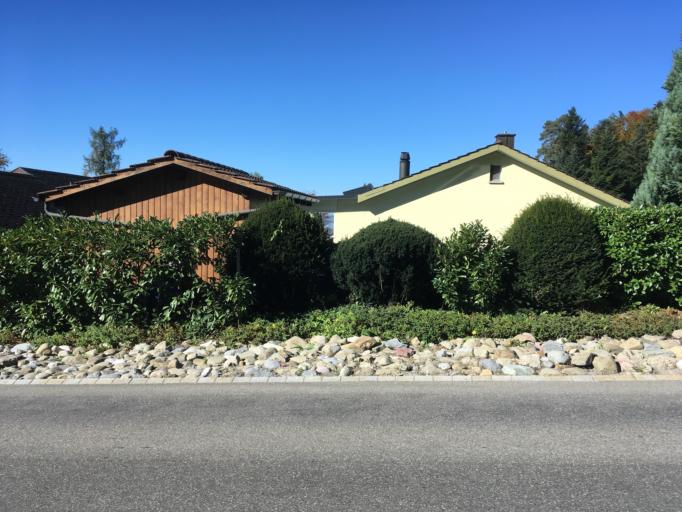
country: CH
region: Zurich
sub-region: Bezirk Hinwil
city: Wetzikon / Kempten
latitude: 47.3266
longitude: 8.8338
